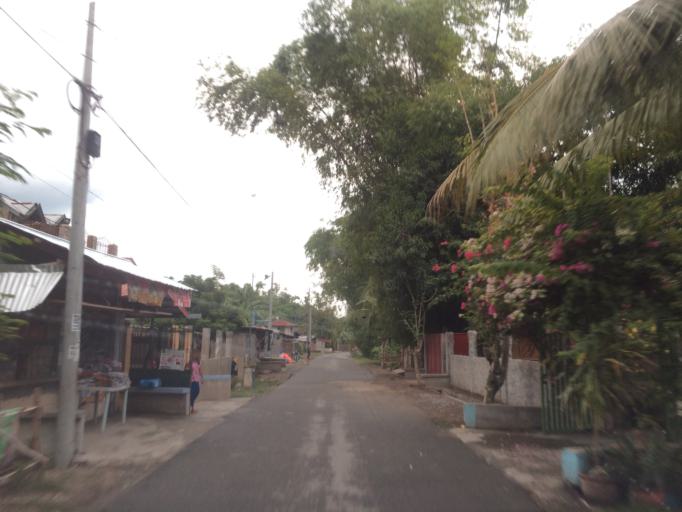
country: PH
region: Ilocos
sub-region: Province of Pangasinan
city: Anambongan
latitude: 15.8718
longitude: 120.3874
